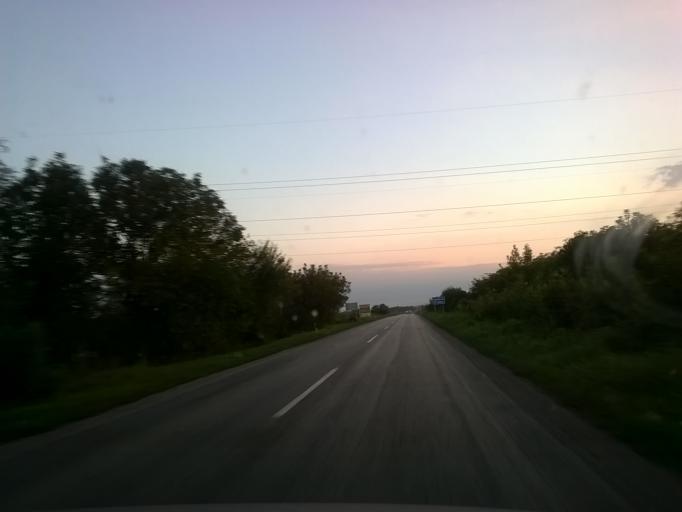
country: RS
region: Autonomna Pokrajina Vojvodina
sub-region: Juznobanatski Okrug
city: Pancevo
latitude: 44.9218
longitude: 20.6595
